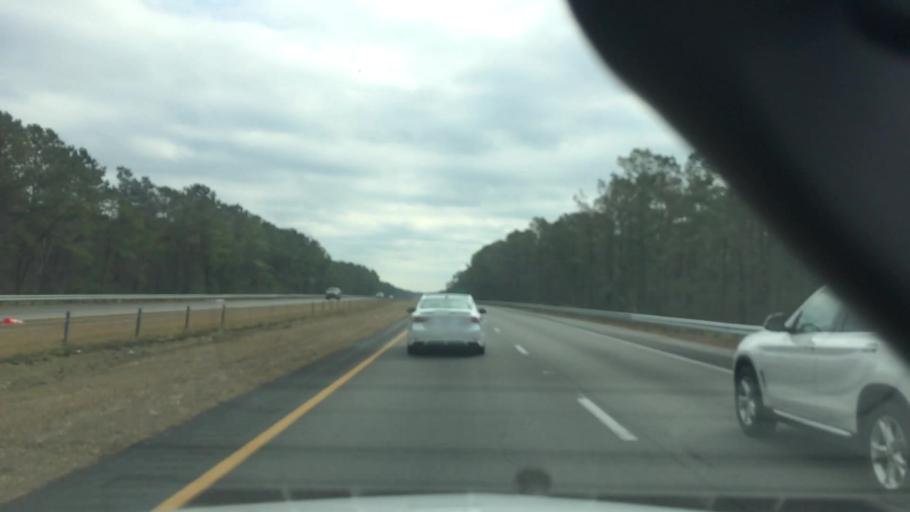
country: US
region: North Carolina
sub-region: New Hanover County
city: Castle Hayne
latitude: 34.3578
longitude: -77.8875
